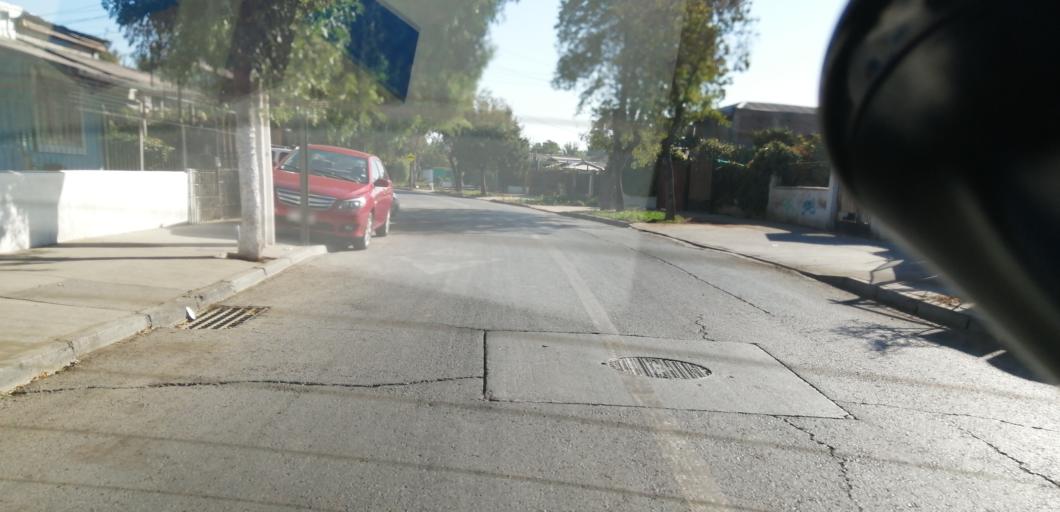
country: CL
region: Santiago Metropolitan
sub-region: Provincia de Santiago
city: Lo Prado
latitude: -33.4407
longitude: -70.7597
